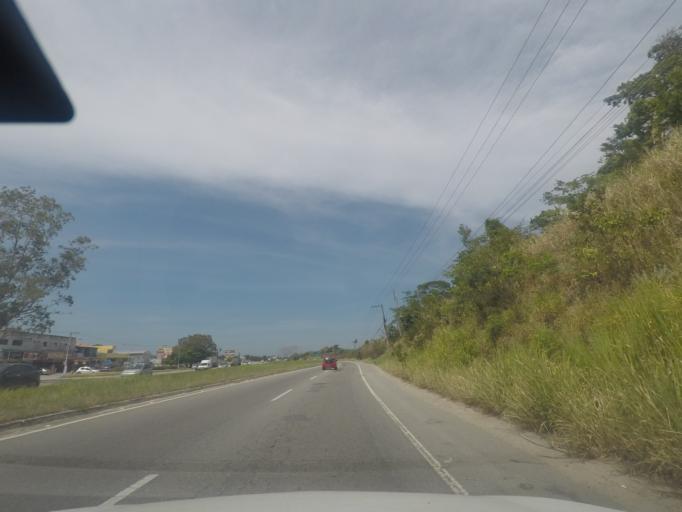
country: BR
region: Rio de Janeiro
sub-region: Marica
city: Marica
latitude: -22.9122
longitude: -42.8437
